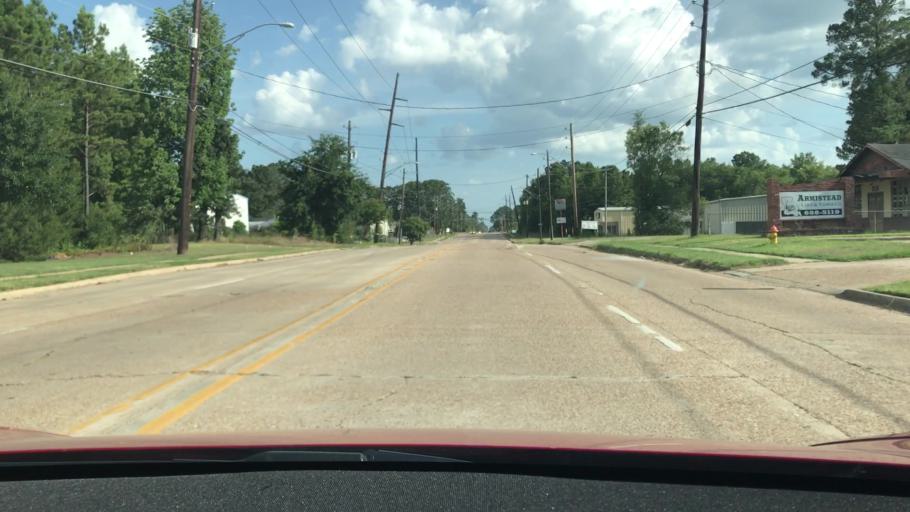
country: US
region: Louisiana
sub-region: Bossier Parish
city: Bossier City
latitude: 32.4164
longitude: -93.7632
